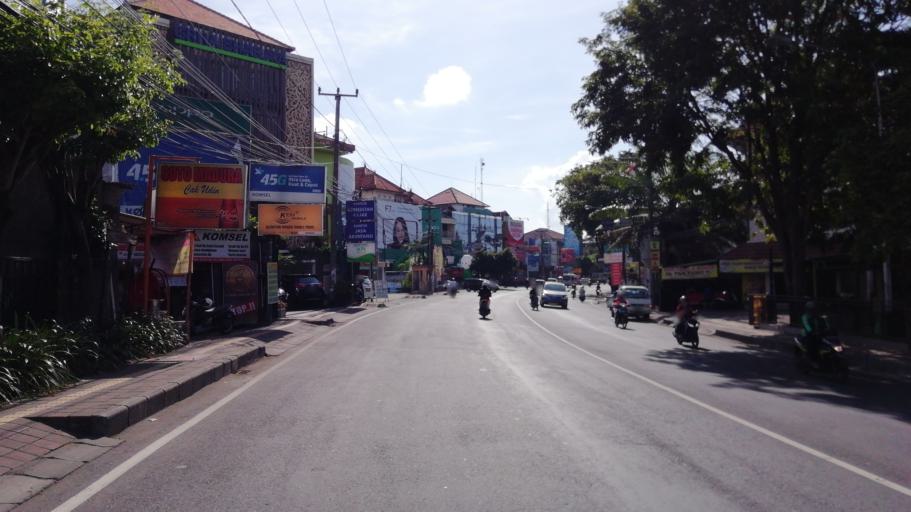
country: ID
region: Bali
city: Denpasar
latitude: -8.6697
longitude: 115.2107
